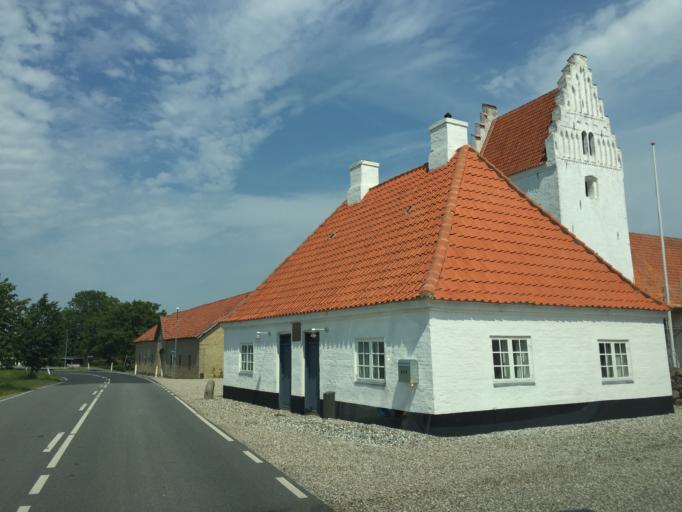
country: DK
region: South Denmark
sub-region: Kerteminde Kommune
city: Kerteminde
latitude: 55.4160
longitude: 10.6606
